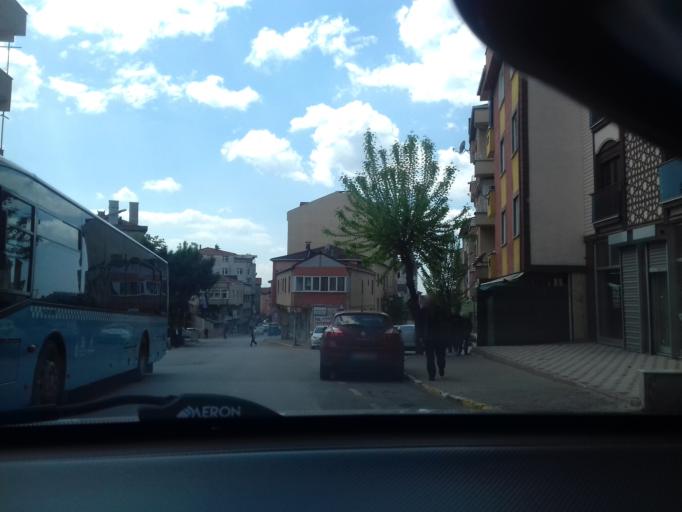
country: TR
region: Istanbul
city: Pendik
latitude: 40.8736
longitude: 29.2824
